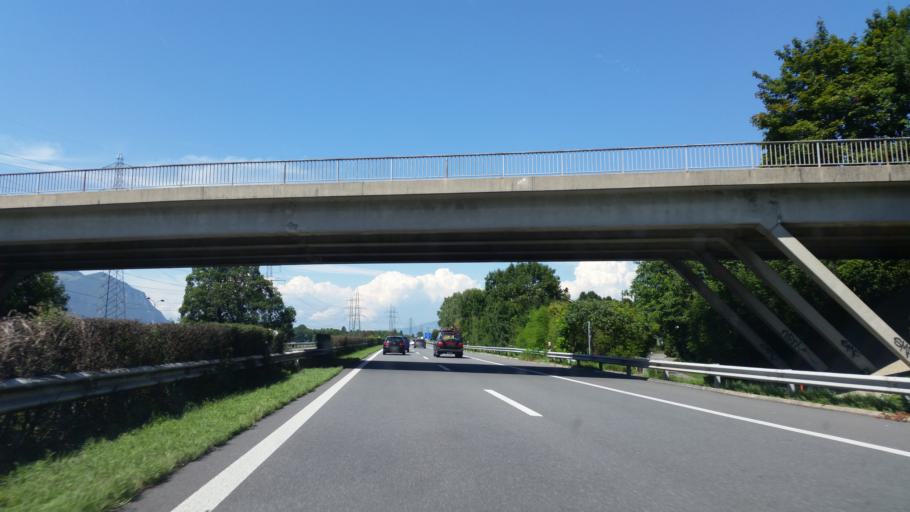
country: CH
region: Vaud
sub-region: Aigle District
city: Aigle
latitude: 46.3140
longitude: 6.9454
